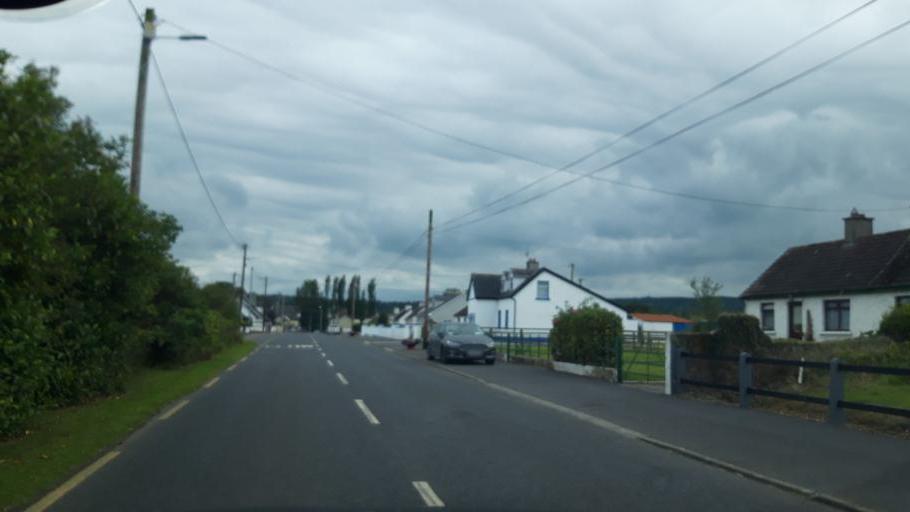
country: IE
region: Leinster
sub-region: Kilkenny
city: Ballyragget
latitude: 52.7365
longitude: -7.3987
